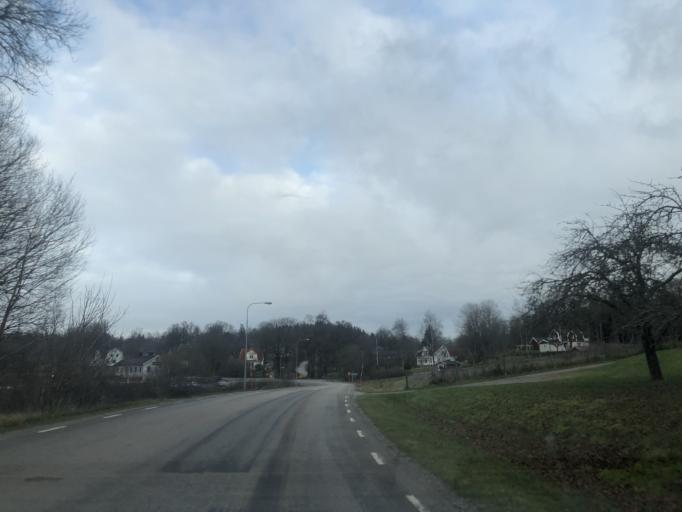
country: SE
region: Vaestra Goetaland
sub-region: Ulricehamns Kommun
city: Ulricehamn
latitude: 57.7192
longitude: 13.3019
